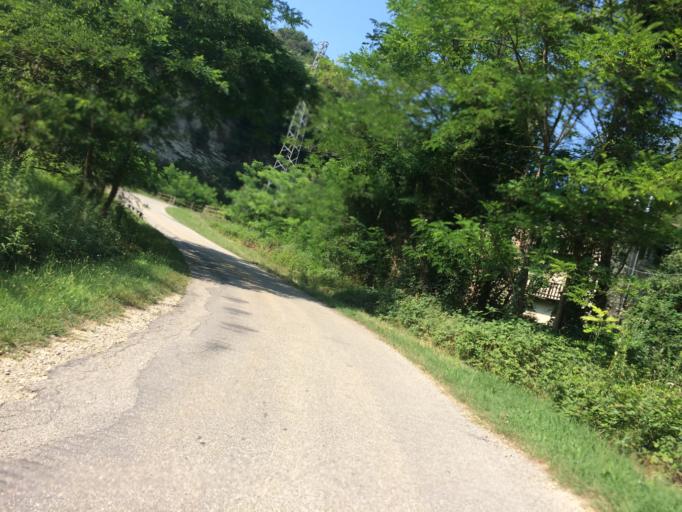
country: IT
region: Piedmont
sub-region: Provincia di Cuneo
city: Cortemilia
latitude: 44.5697
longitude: 8.2065
